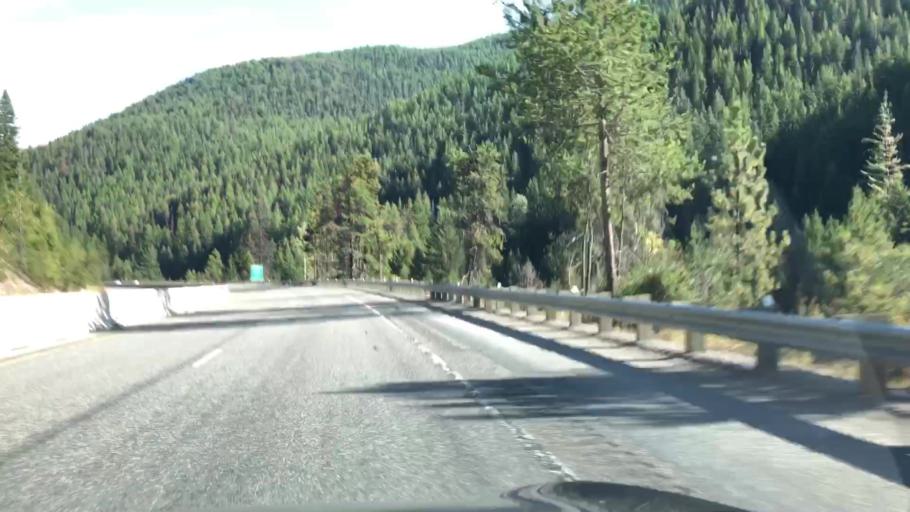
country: US
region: Montana
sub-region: Sanders County
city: Thompson Falls
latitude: 47.3959
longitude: -115.4550
